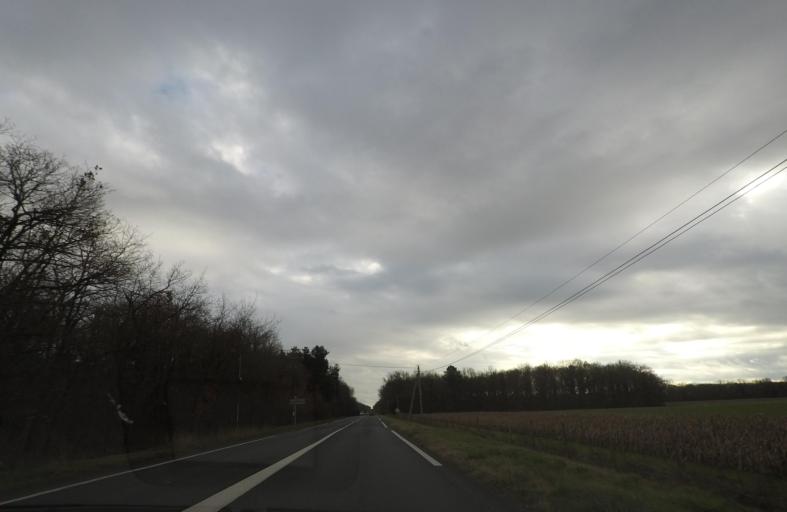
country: FR
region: Centre
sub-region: Departement du Loir-et-Cher
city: Soings-en-Sologne
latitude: 47.4306
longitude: 1.5660
